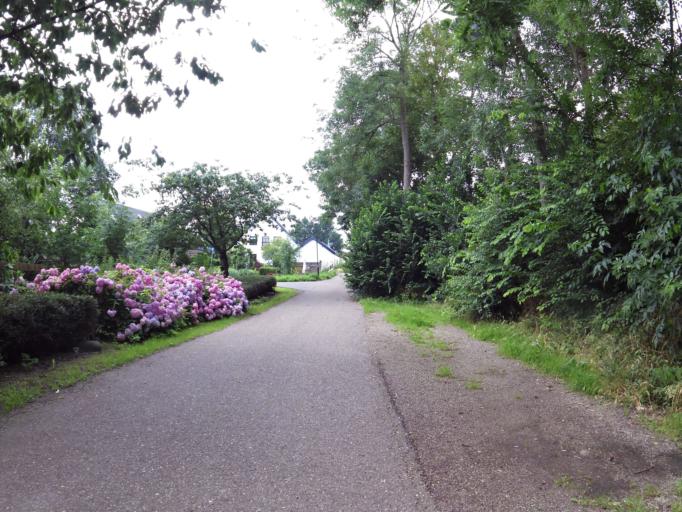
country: NL
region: South Holland
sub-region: Gemeente Gorinchem
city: Gorinchem
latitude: 51.8838
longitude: 4.9460
